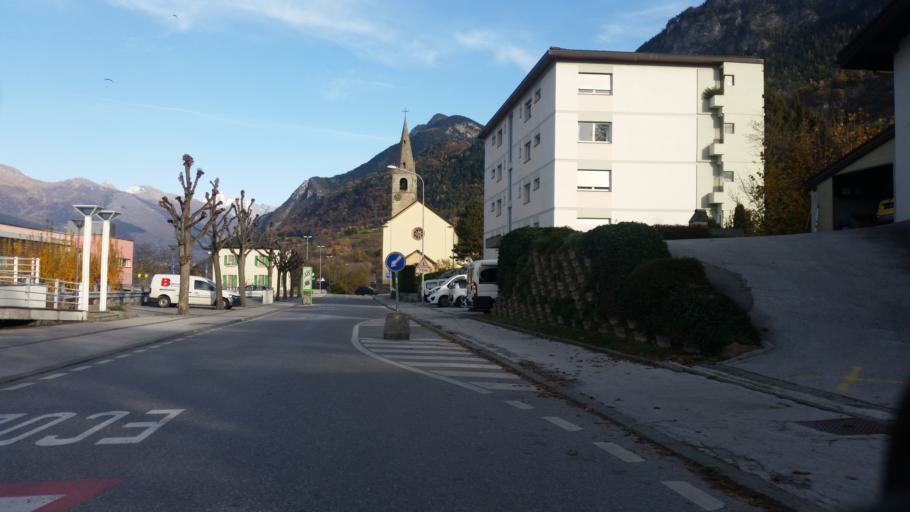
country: CH
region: Valais
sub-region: Sierre District
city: Chalais
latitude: 46.2649
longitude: 7.5023
